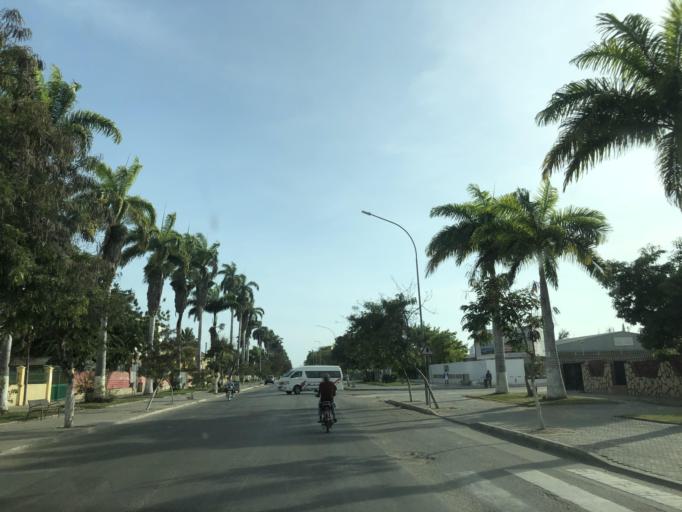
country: AO
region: Benguela
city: Benguela
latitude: -12.5734
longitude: 13.4018
